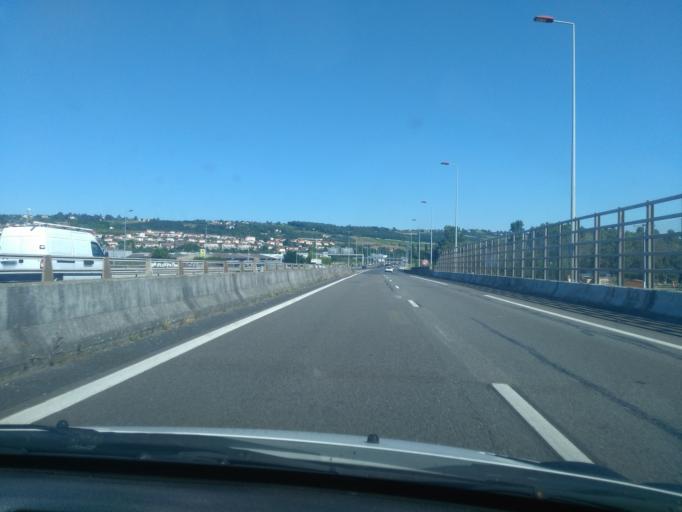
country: FR
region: Rhone-Alpes
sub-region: Departement du Rhone
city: Anse
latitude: 45.9378
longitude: 4.7259
